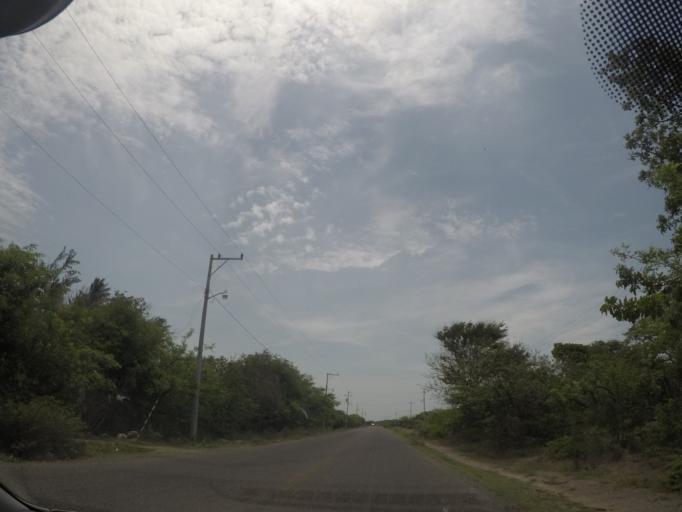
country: MX
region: Oaxaca
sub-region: San Mateo del Mar
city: Colonia Juarez
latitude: 16.2075
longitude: -95.0090
